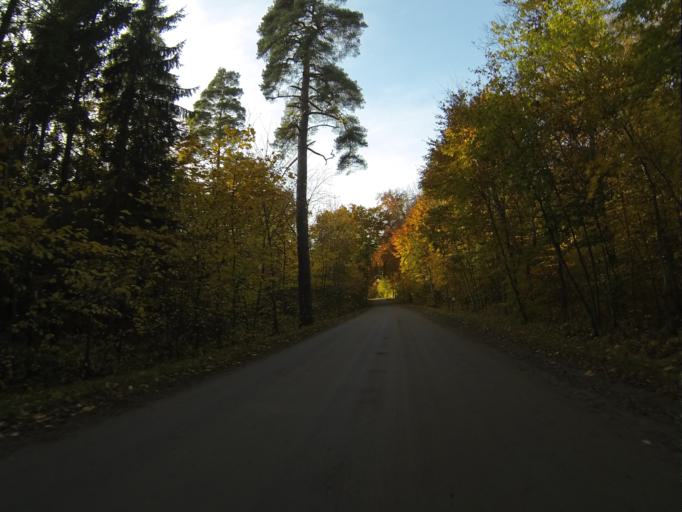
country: SE
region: Skane
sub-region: Lunds Kommun
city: Veberod
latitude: 55.6875
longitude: 13.4708
